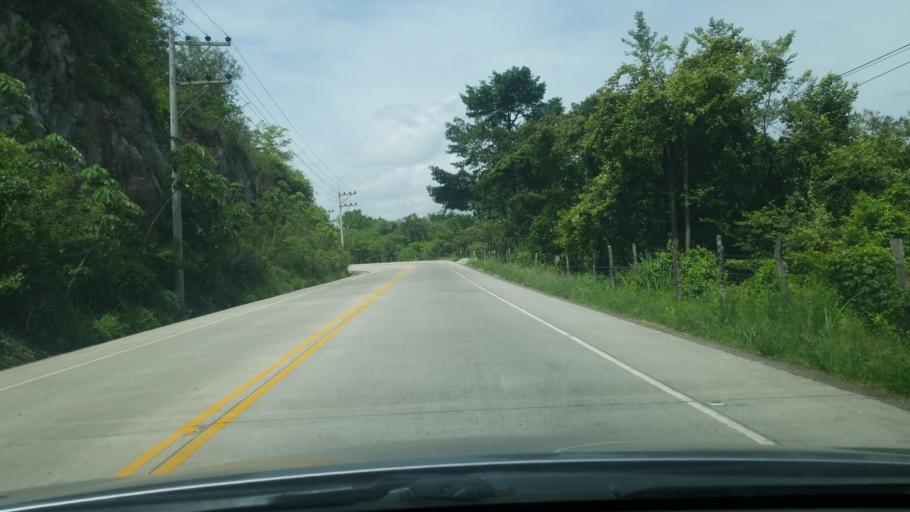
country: HN
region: Copan
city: La Entrada
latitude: 15.0386
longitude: -88.7654
